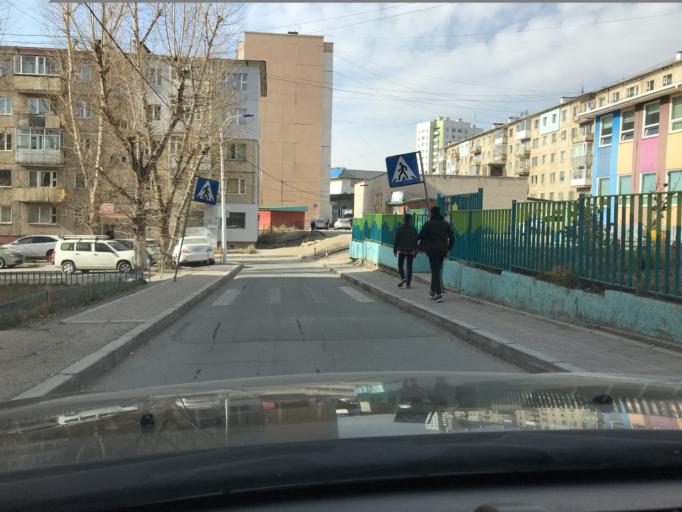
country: MN
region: Ulaanbaatar
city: Ulaanbaatar
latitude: 47.9225
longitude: 106.9445
